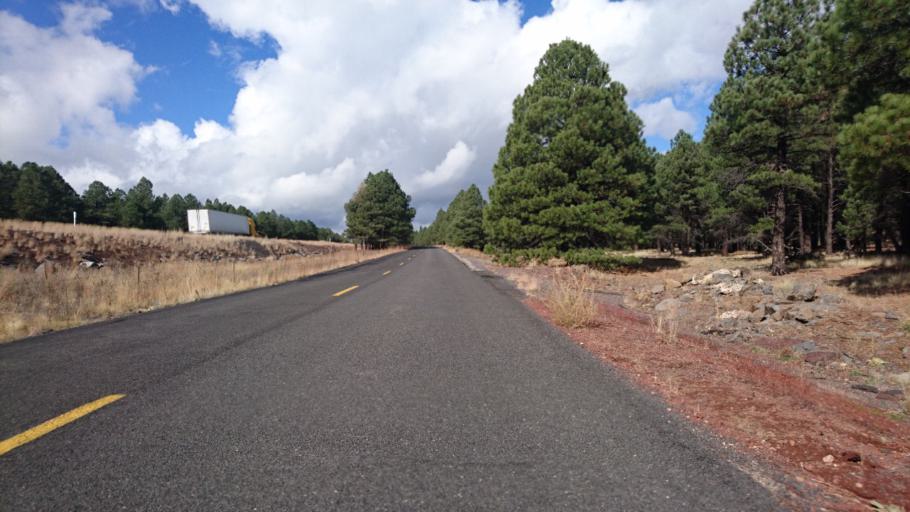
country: US
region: Arizona
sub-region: Coconino County
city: Parks
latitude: 35.2463
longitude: -111.8428
